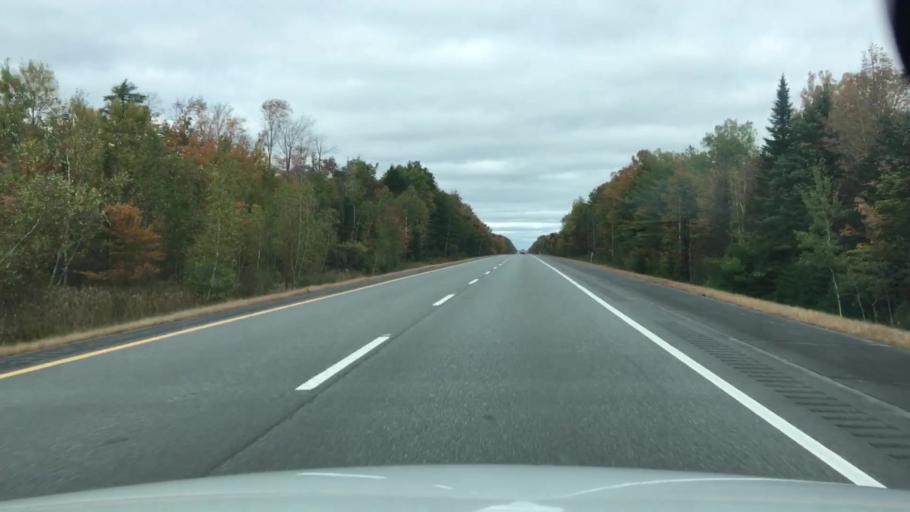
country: US
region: Maine
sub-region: Waldo County
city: Burnham
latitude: 44.7172
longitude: -69.4447
